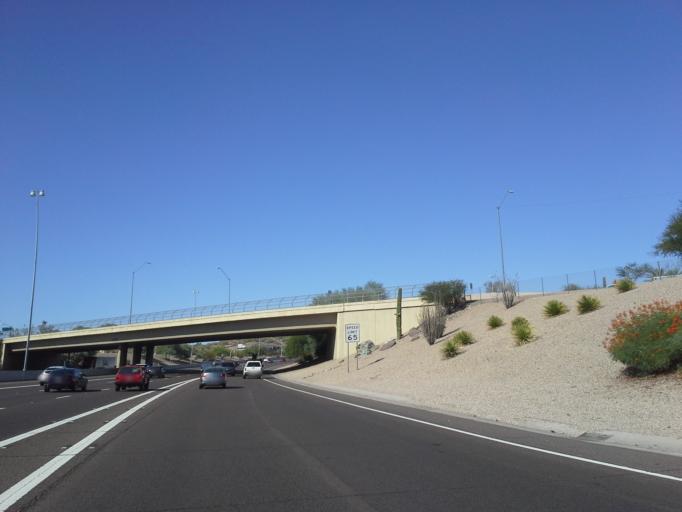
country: US
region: Arizona
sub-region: Maricopa County
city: Paradise Valley
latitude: 33.5778
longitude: -112.0121
